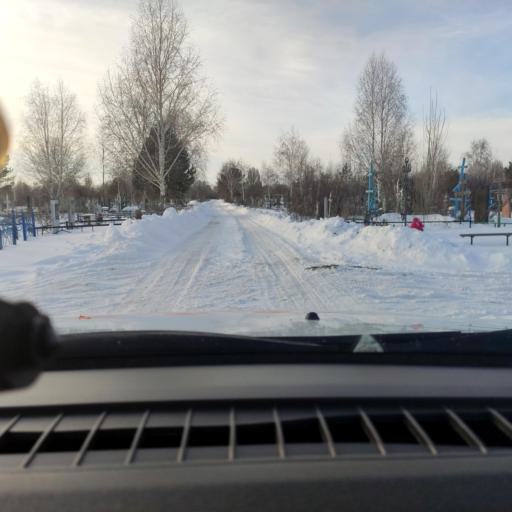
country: RU
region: Samara
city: Chapayevsk
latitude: 52.9893
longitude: 49.7507
